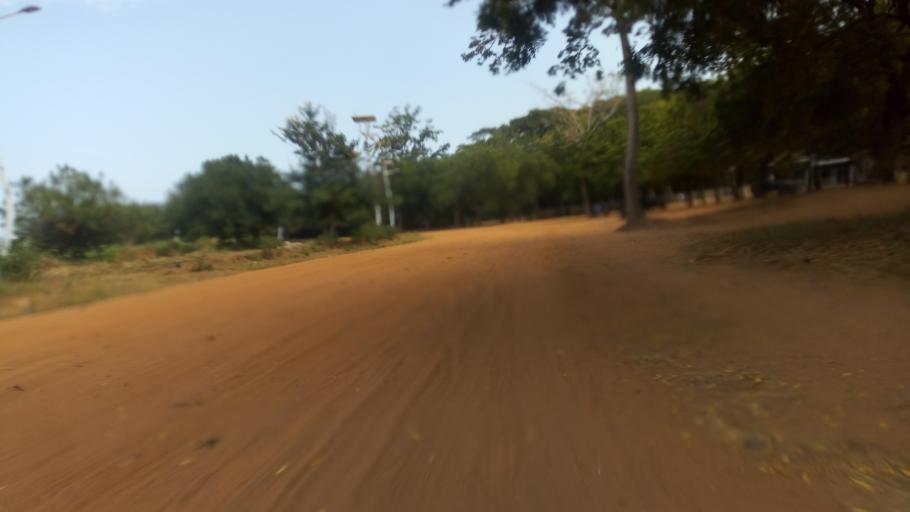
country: TG
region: Maritime
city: Lome
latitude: 6.1781
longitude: 1.2133
